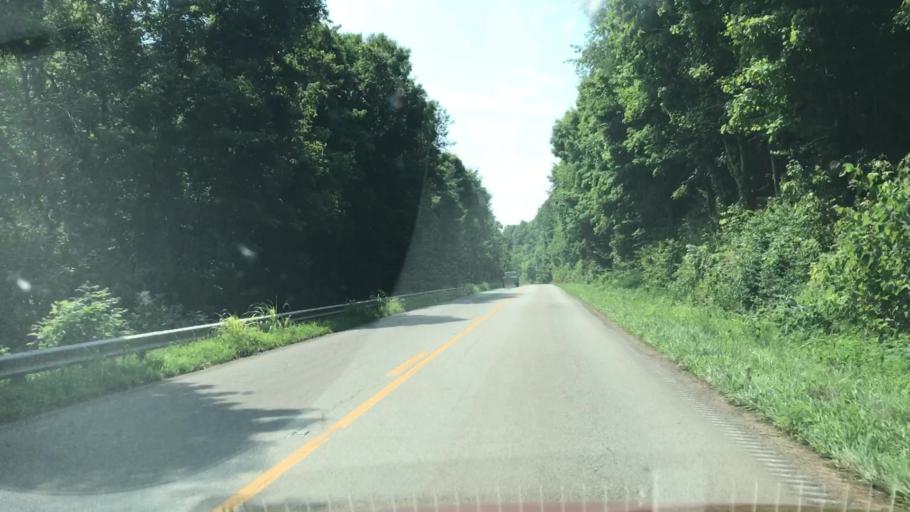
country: US
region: Kentucky
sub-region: Barren County
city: Glasgow
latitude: 36.8626
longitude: -85.8458
